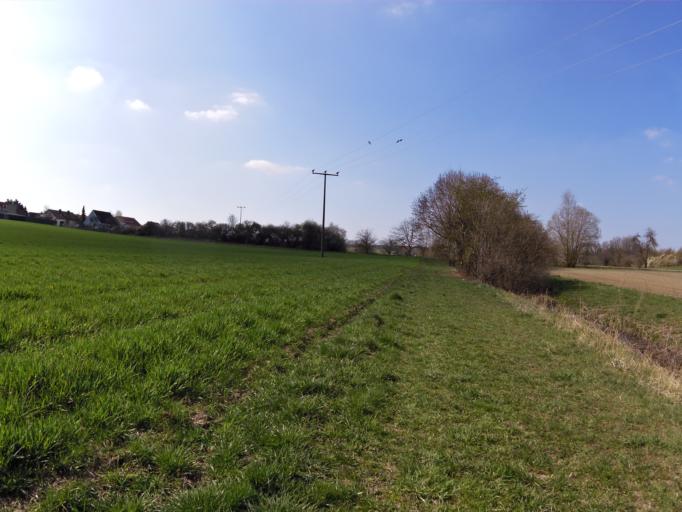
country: DE
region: Bavaria
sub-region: Regierungsbezirk Unterfranken
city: Biebelried
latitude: 49.7336
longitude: 10.0892
